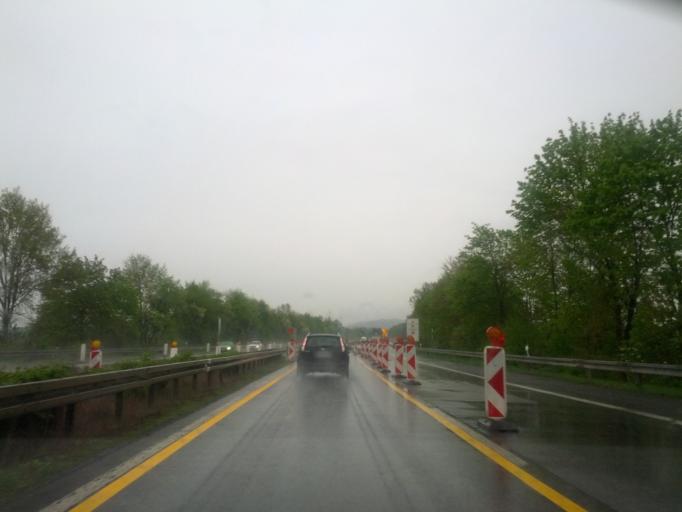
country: DE
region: Hesse
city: Lollar
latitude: 50.6228
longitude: 8.6795
